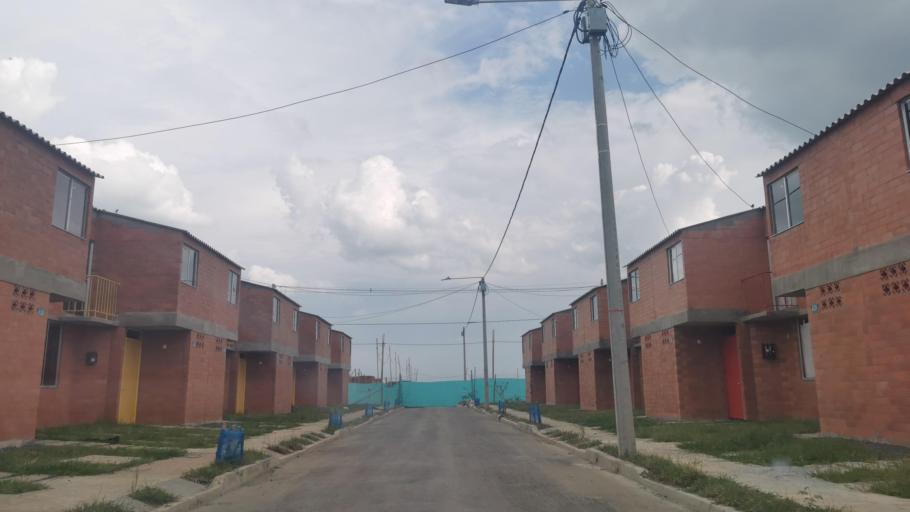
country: CO
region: Valle del Cauca
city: Jamundi
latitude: 3.2317
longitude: -76.5255
